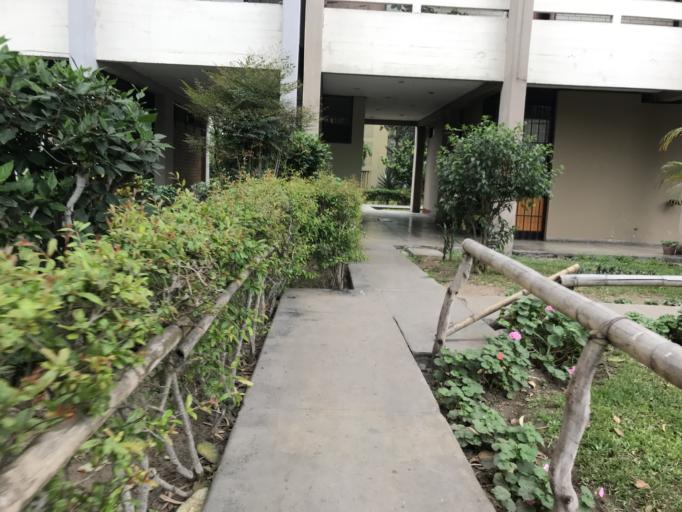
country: PE
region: Lima
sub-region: Lima
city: San Isidro
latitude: -12.0863
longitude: -77.0512
